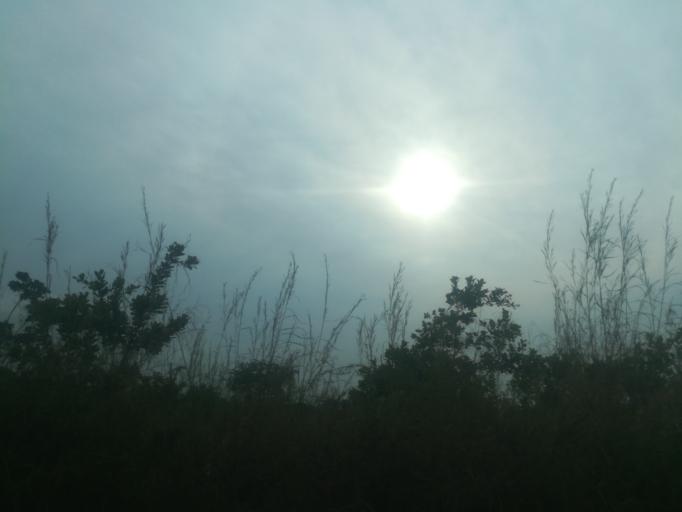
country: NG
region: Ogun
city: Ayetoro
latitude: 7.2491
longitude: 3.1192
